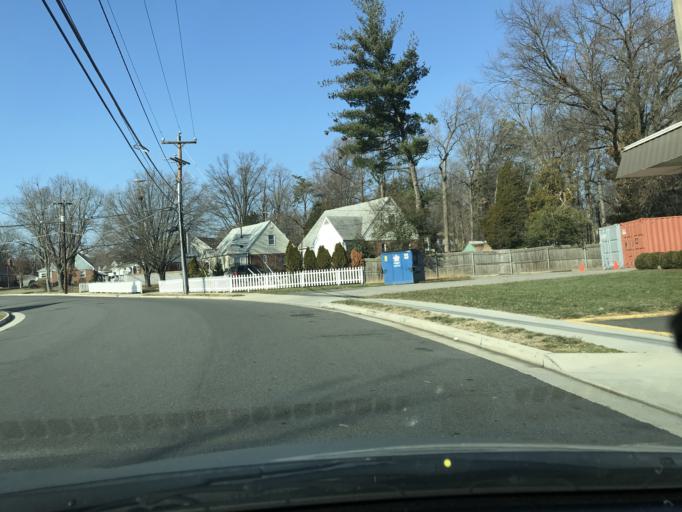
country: US
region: Virginia
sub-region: City of Fairfax
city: Fairfax
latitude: 38.8547
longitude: -77.3185
